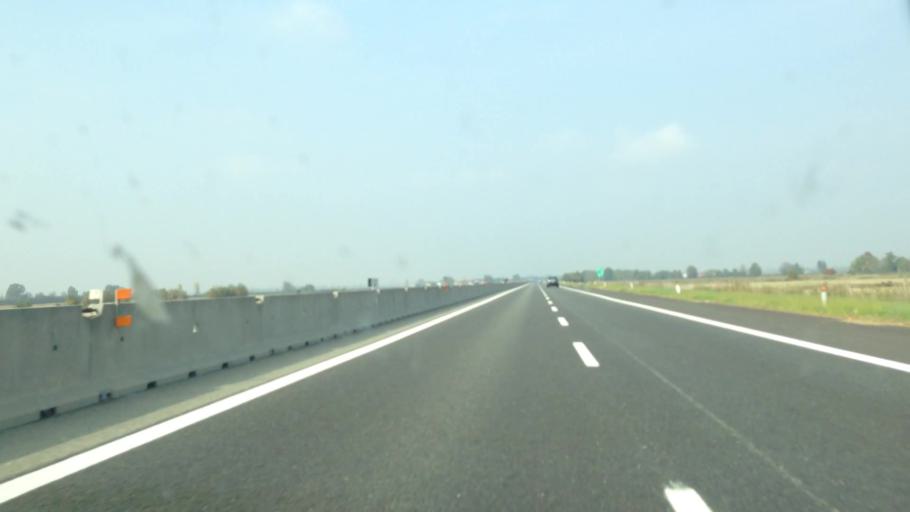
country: IT
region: Piedmont
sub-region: Provincia di Vercelli
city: Salasco
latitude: 45.3177
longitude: 8.2647
